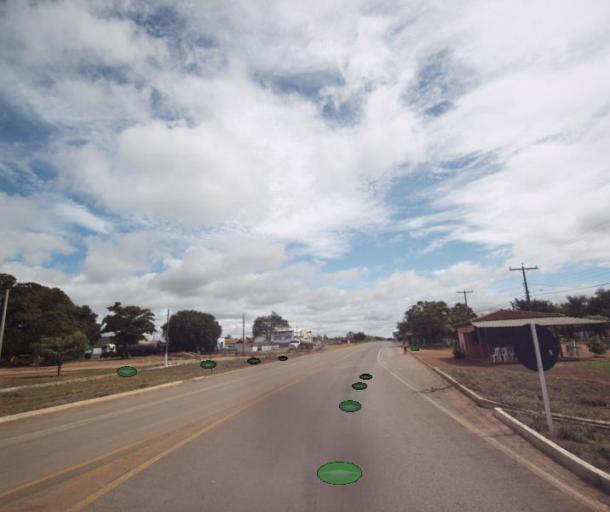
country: BR
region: Goias
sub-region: Barro Alto
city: Barro Alto
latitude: -15.2081
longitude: -48.6999
